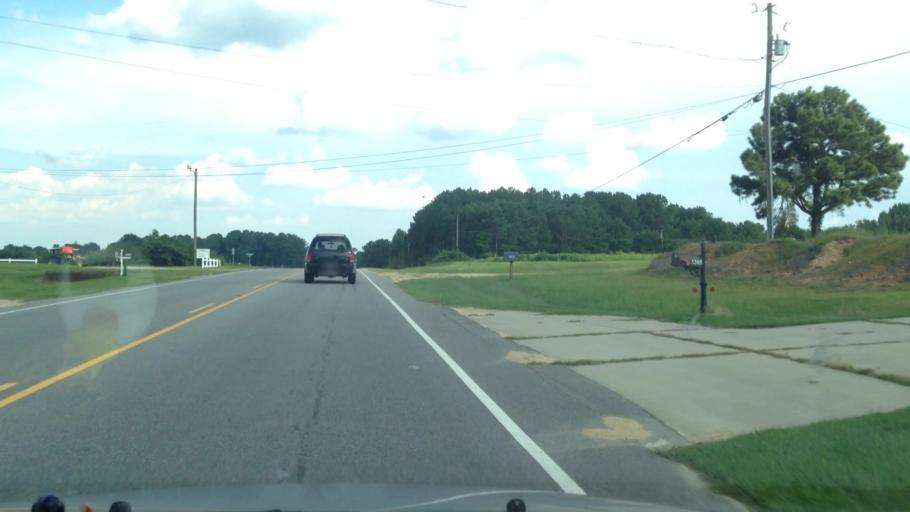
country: US
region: North Carolina
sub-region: Harnett County
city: Lillington
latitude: 35.4151
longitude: -78.8691
